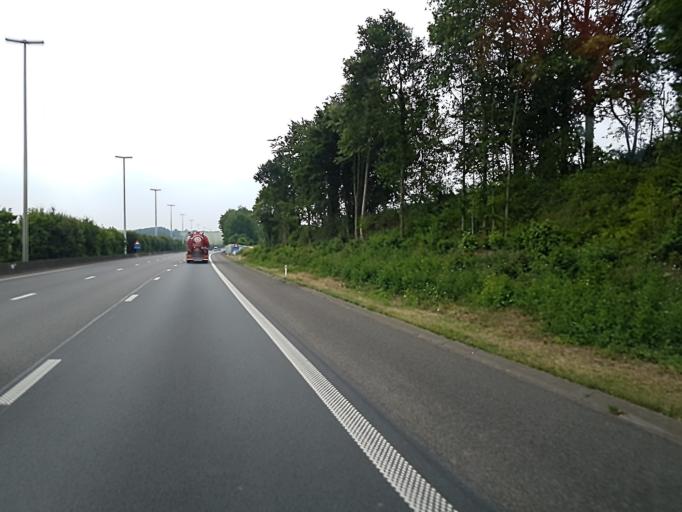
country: BE
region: Wallonia
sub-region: Province de Liege
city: Lincent
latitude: 50.7186
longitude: 5.0086
